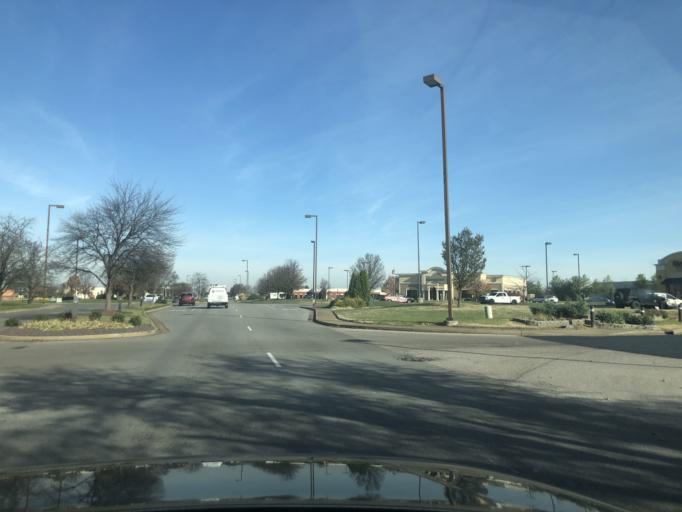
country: US
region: Indiana
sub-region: Warrick County
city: Newburgh
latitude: 37.9774
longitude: -87.4626
